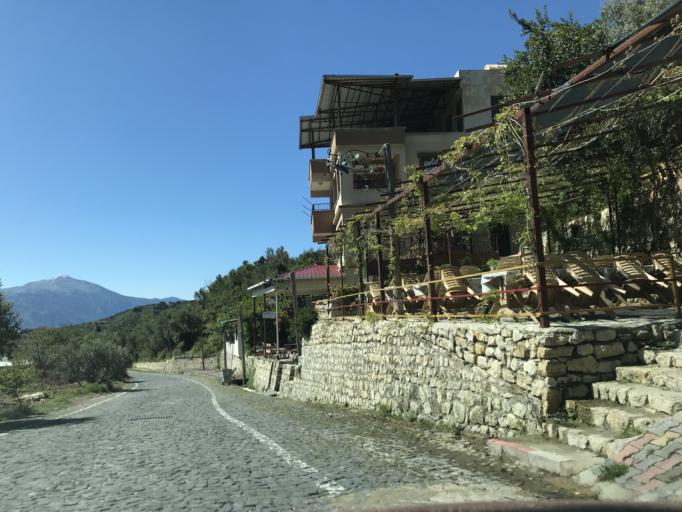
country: TR
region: Hatay
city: Samandag
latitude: 36.1324
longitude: 35.9739
